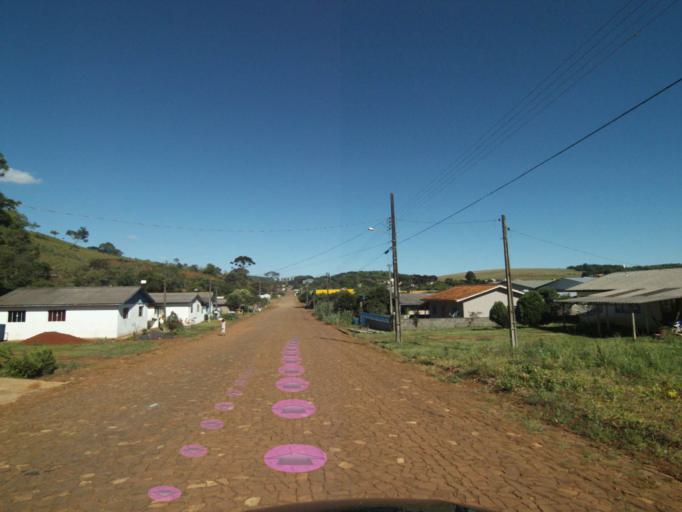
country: BR
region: Parana
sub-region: Coronel Vivida
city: Coronel Vivida
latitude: -26.1413
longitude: -52.3870
